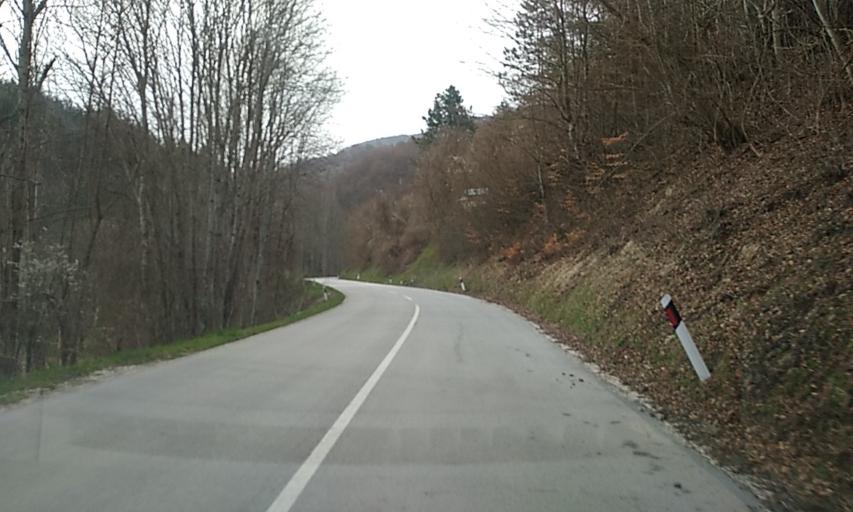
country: RS
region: Central Serbia
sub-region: Pcinjski Okrug
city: Bosilegrad
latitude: 42.5389
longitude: 22.4109
